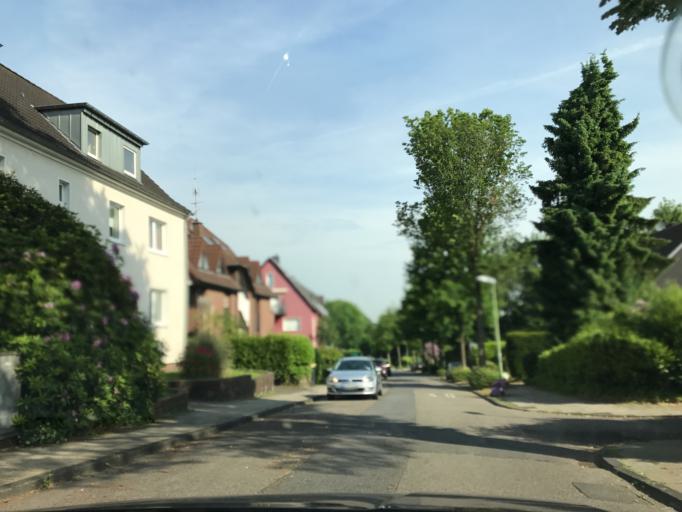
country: DE
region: North Rhine-Westphalia
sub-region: Regierungsbezirk Dusseldorf
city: Essen
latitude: 51.4150
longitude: 6.9905
